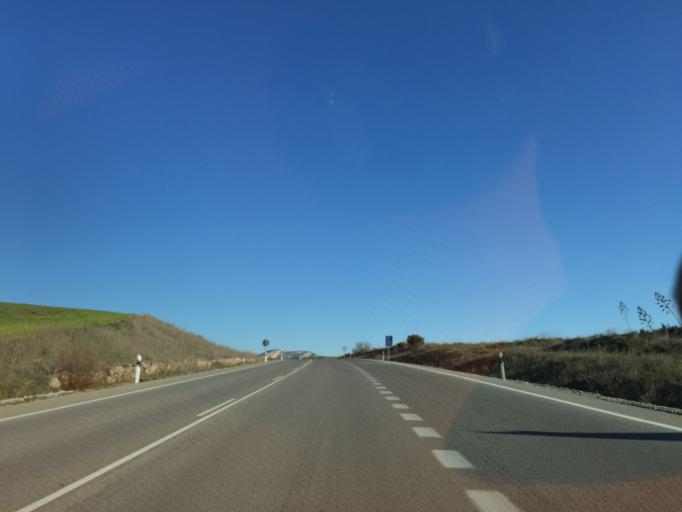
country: ES
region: Andalusia
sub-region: Provincia de Malaga
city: Ardales
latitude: 36.9138
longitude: -4.8416
